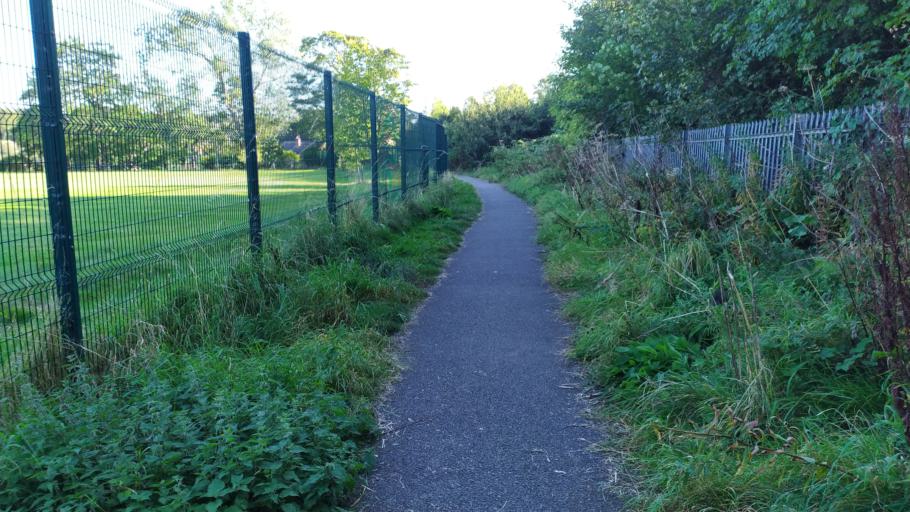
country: GB
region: England
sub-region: City and Borough of Leeds
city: Chapel Allerton
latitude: 53.8327
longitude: -1.5572
